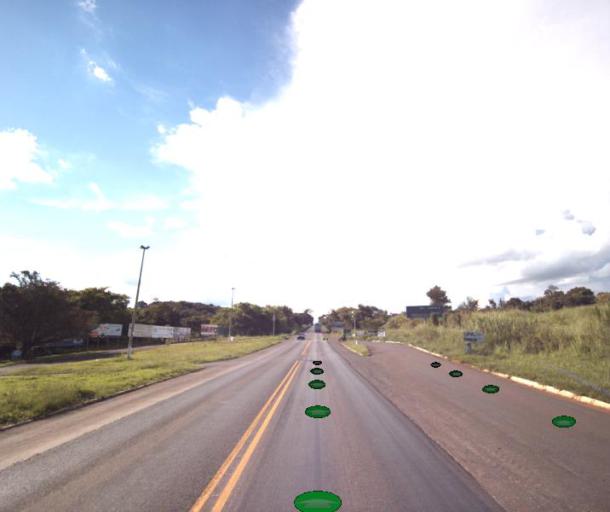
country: BR
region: Goias
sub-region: Rialma
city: Rialma
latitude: -15.3329
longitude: -49.5703
